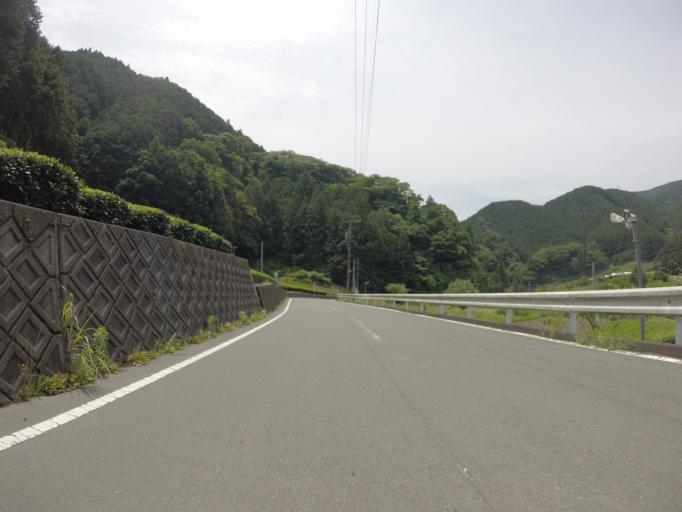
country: JP
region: Shizuoka
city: Shizuoka-shi
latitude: 35.0333
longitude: 138.2897
